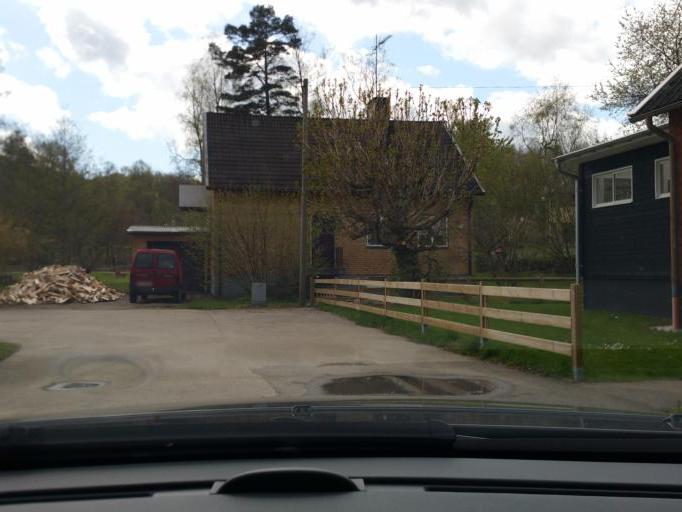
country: SE
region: Kronoberg
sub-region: Vaxjo Kommun
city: Lammhult
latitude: 57.1726
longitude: 14.5744
